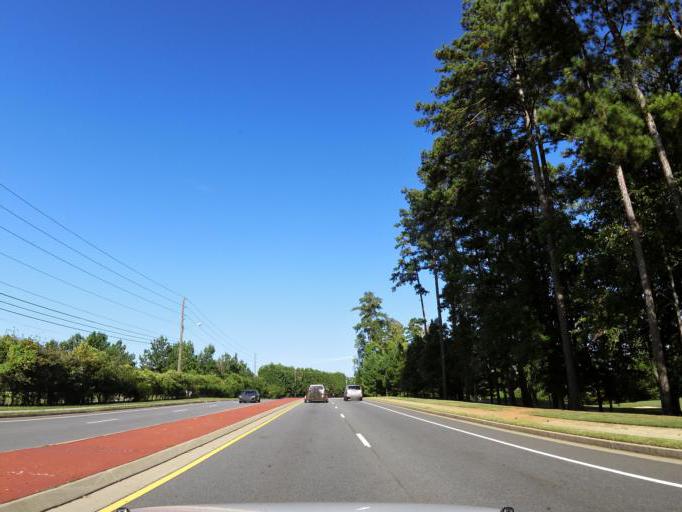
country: US
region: Georgia
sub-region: Cobb County
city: Kennesaw
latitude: 33.9862
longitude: -84.6199
